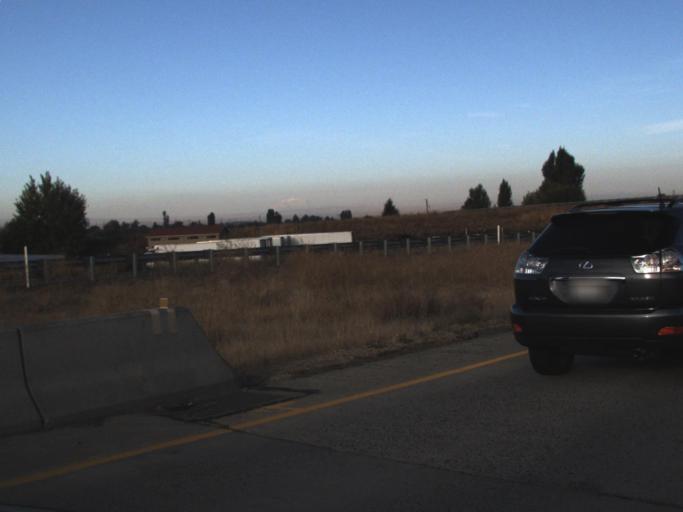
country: US
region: Washington
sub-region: Yakima County
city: Grandview
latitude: 46.2628
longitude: -119.8918
